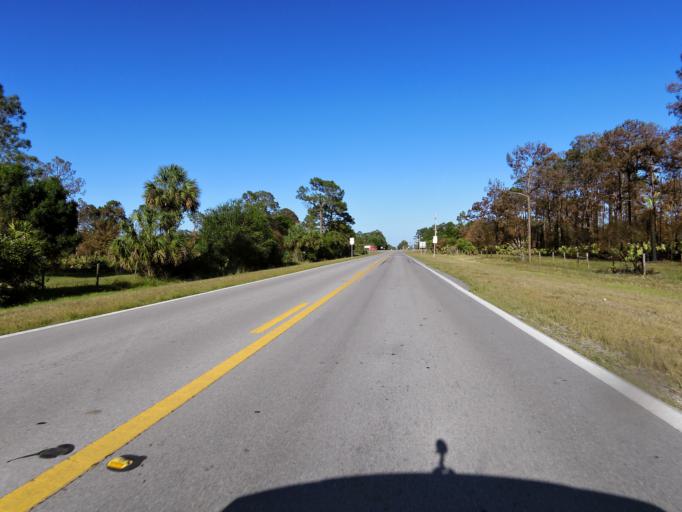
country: US
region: Florida
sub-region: Collier County
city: Immokalee
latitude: 26.3032
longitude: -81.3457
